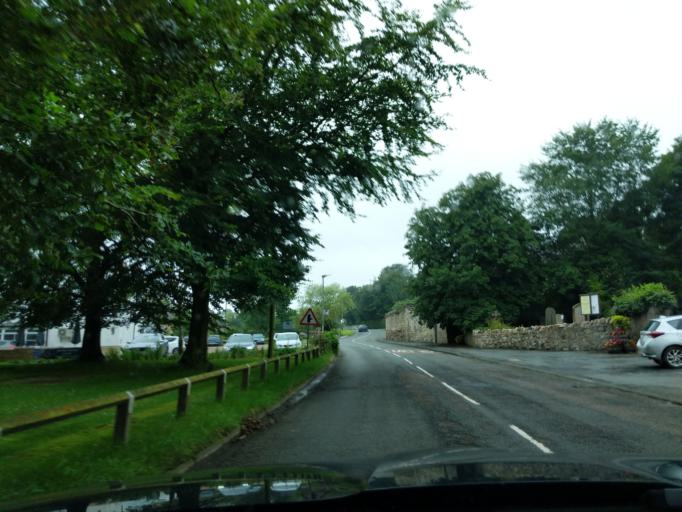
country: GB
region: England
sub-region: Northumberland
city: Lowick
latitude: 55.6499
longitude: -1.9816
